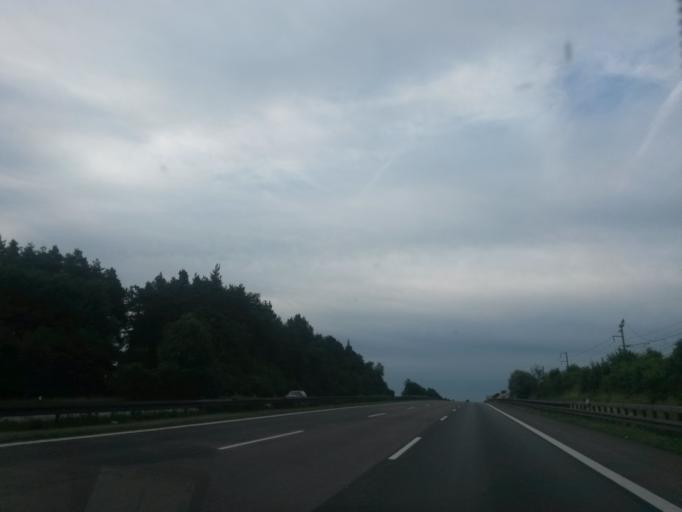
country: DE
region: Bavaria
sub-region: Regierungsbezirk Mittelfranken
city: Allersberg
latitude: 49.2045
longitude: 11.2369
